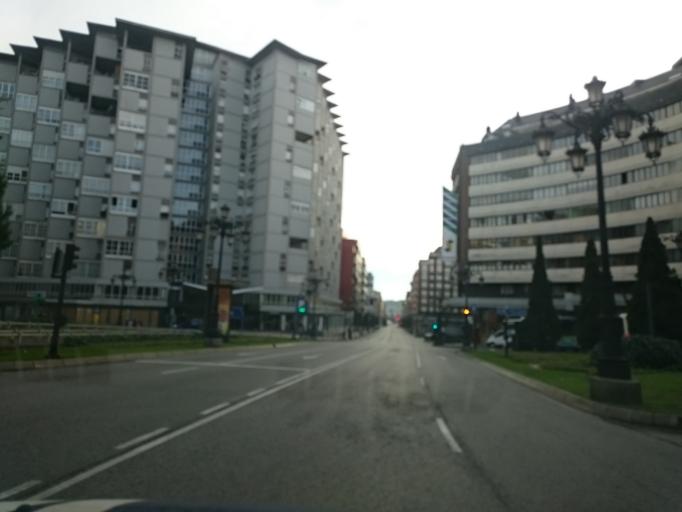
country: ES
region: Asturias
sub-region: Province of Asturias
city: Oviedo
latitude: 43.3635
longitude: -5.8390
